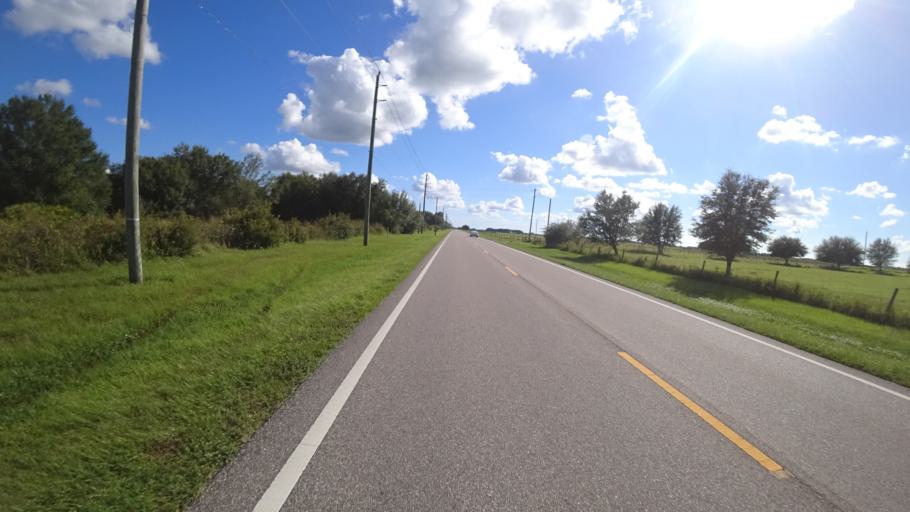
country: US
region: Florida
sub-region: Sarasota County
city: Lake Sarasota
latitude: 27.3721
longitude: -82.2683
